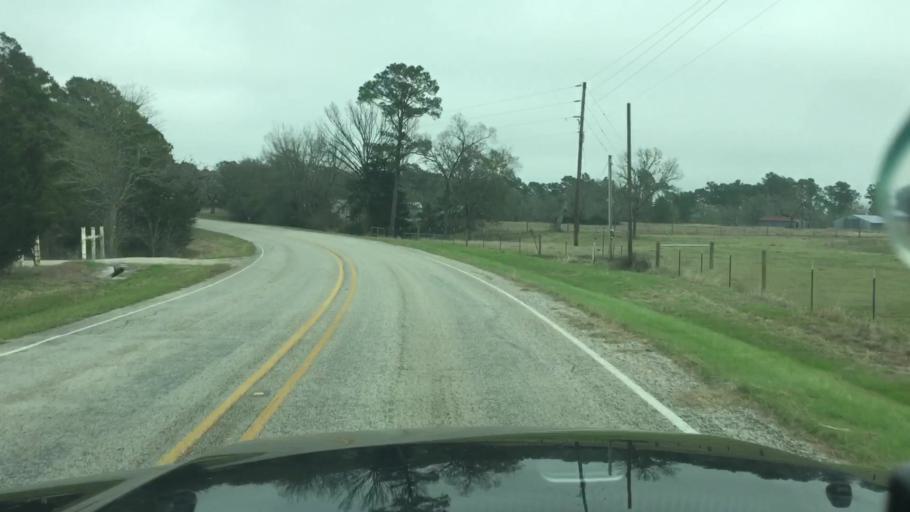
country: US
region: Texas
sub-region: Fayette County
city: La Grange
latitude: 30.0123
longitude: -96.9287
